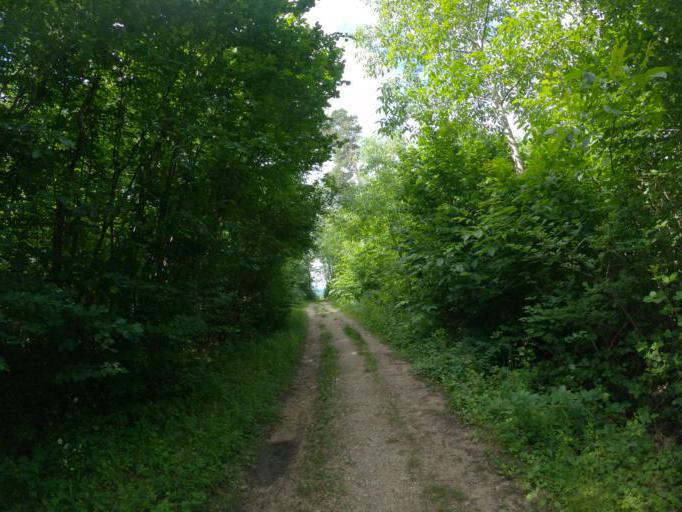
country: DE
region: Baden-Wuerttemberg
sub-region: Regierungsbezirk Stuttgart
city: Schlierbach
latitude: 48.6901
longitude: 9.5228
